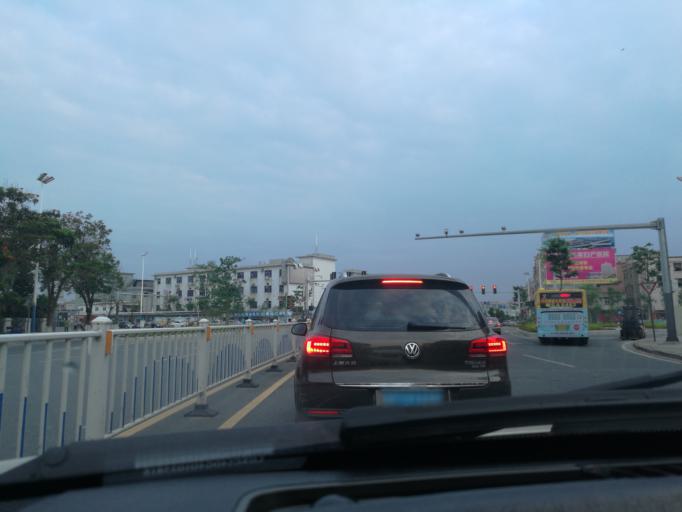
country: CN
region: Guangdong
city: Changping
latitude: 23.0152
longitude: 113.9895
